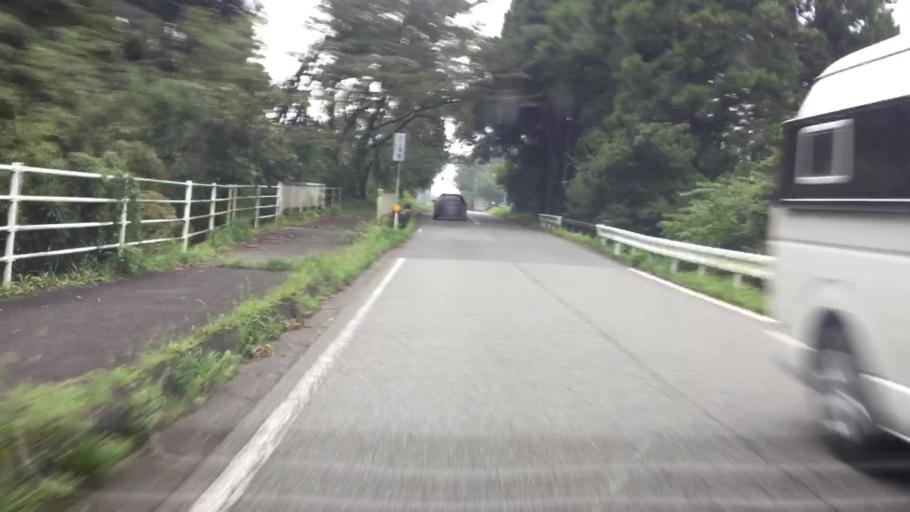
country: JP
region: Shizuoka
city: Fujinomiya
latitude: 35.3470
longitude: 138.5956
